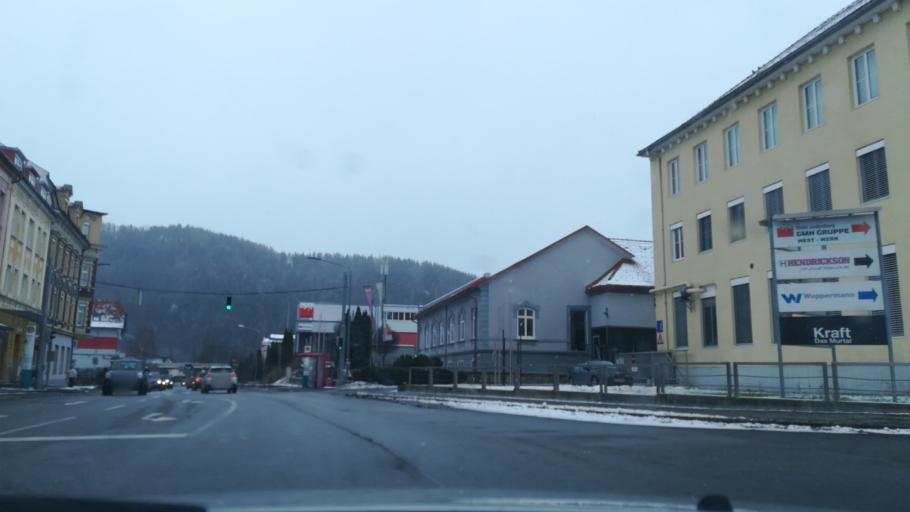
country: AT
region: Styria
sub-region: Politischer Bezirk Murtal
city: Judenburg
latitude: 47.1751
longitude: 14.6654
